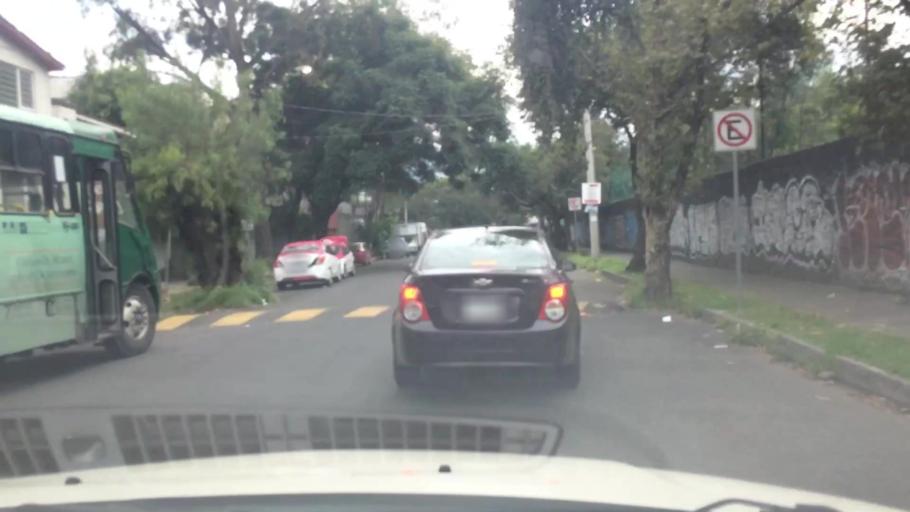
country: MX
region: Mexico City
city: Tlalpan
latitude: 19.2977
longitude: -99.1577
